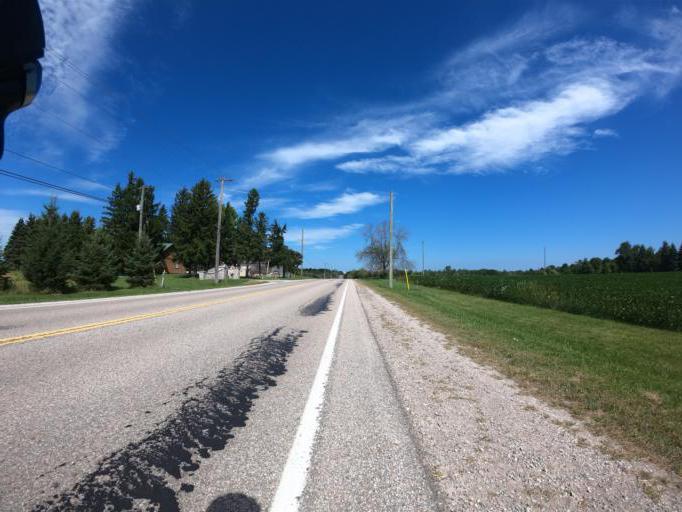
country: CA
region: Ontario
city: Waterloo
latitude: 43.5200
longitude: -80.3984
